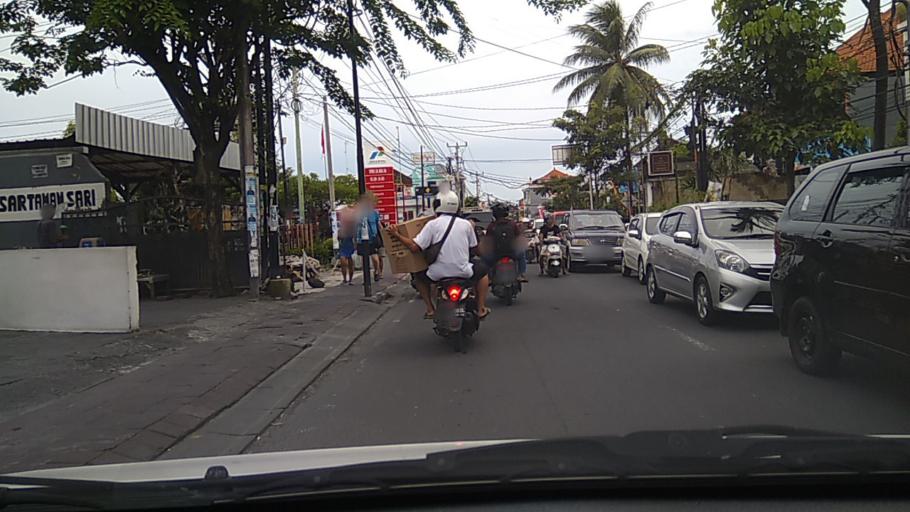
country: ID
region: Bali
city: Kuta
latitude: -8.6725
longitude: 115.1650
